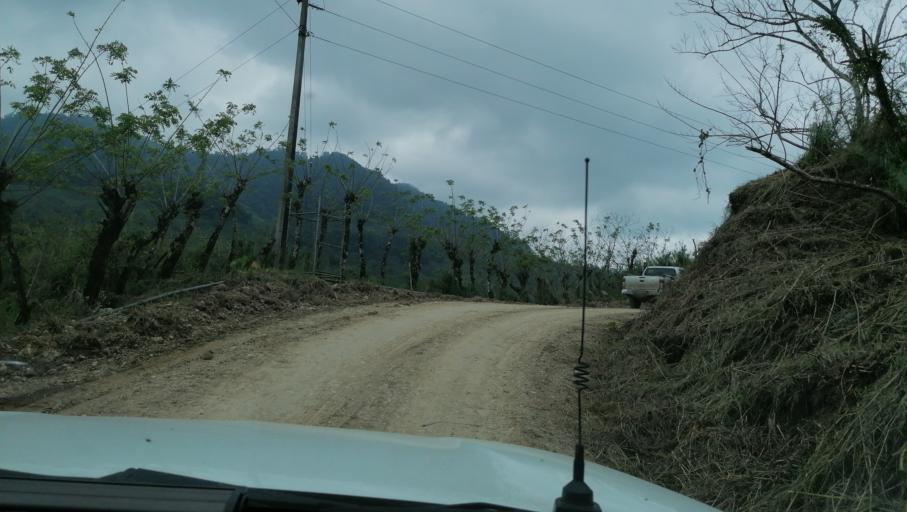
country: MX
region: Chiapas
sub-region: Ocotepec
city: San Pablo Huacano
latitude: 17.2685
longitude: -93.2574
